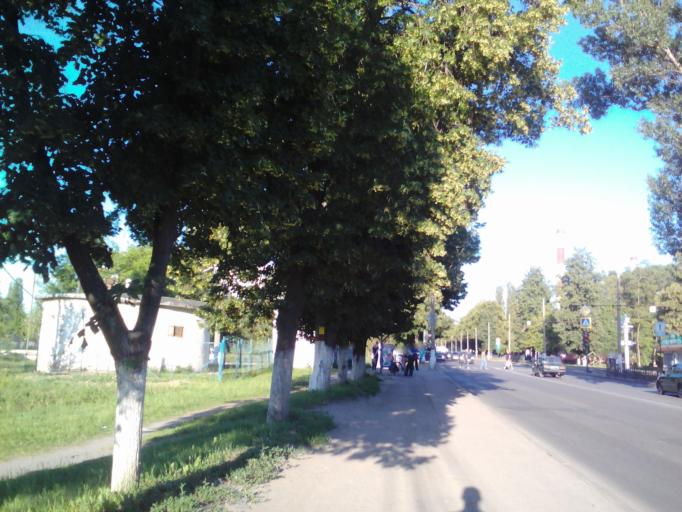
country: RU
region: Kursk
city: Voroshnevo
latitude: 51.6674
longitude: 36.1013
